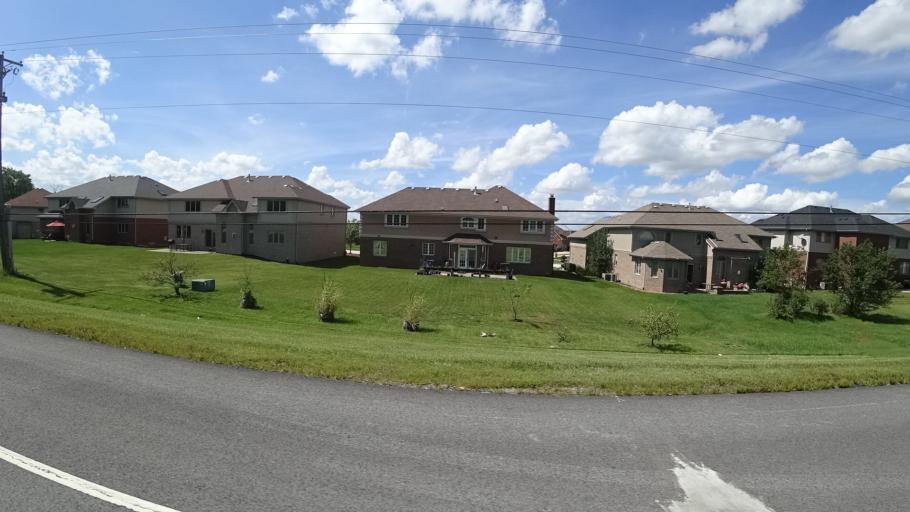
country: US
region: Illinois
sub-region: Cook County
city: Country Club Hills
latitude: 41.5474
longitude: -87.7329
